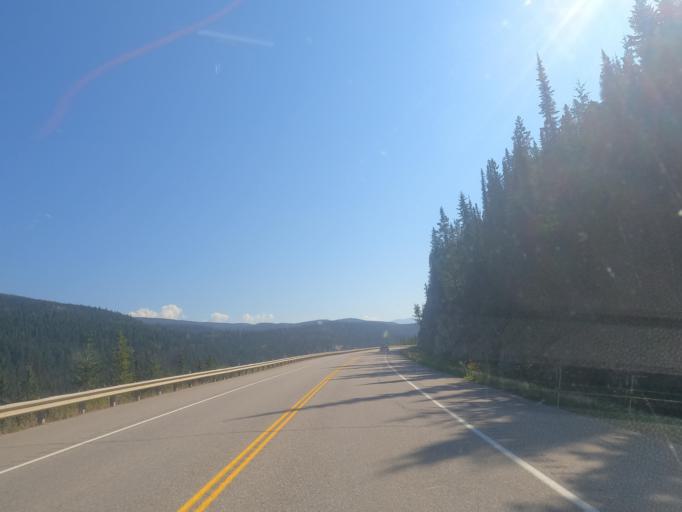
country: CA
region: Alberta
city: Jasper Park Lodge
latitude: 52.8729
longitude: -118.2863
